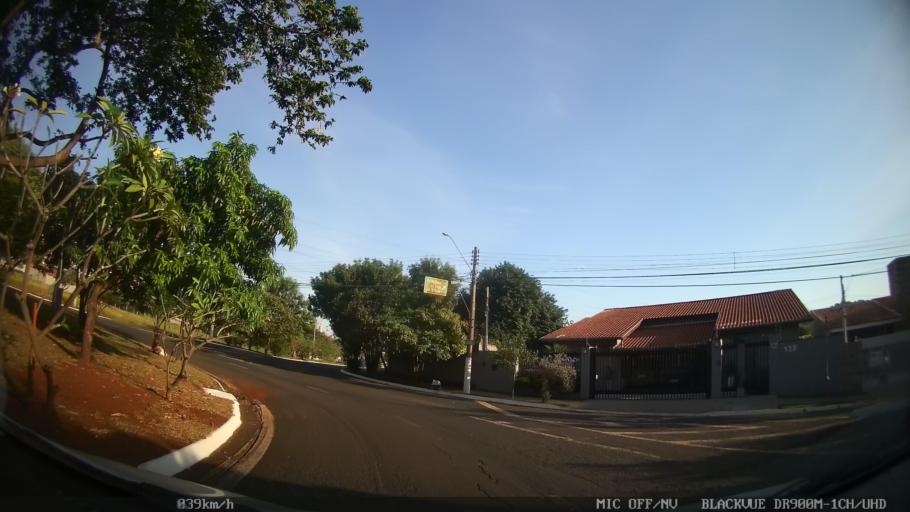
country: BR
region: Sao Paulo
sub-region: Ribeirao Preto
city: Ribeirao Preto
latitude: -21.2120
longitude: -47.7853
